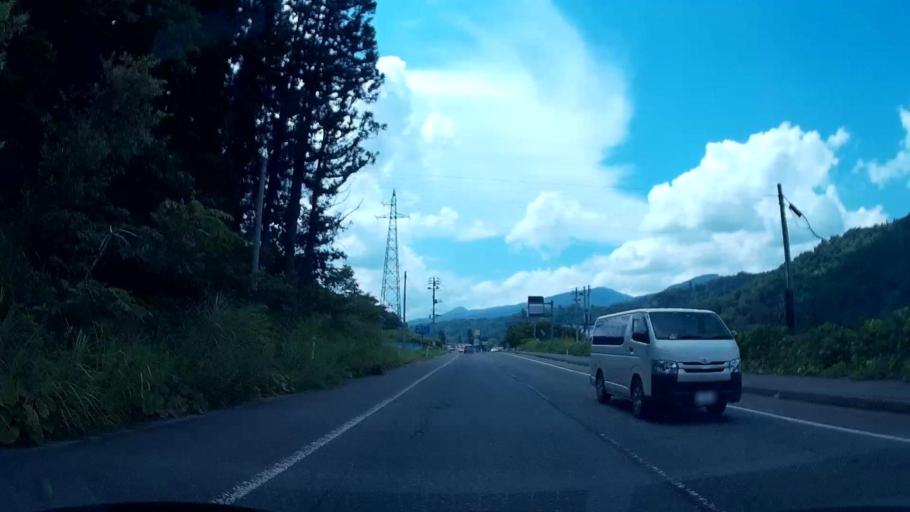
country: JP
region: Niigata
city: Tokamachi
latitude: 37.0027
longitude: 138.6377
